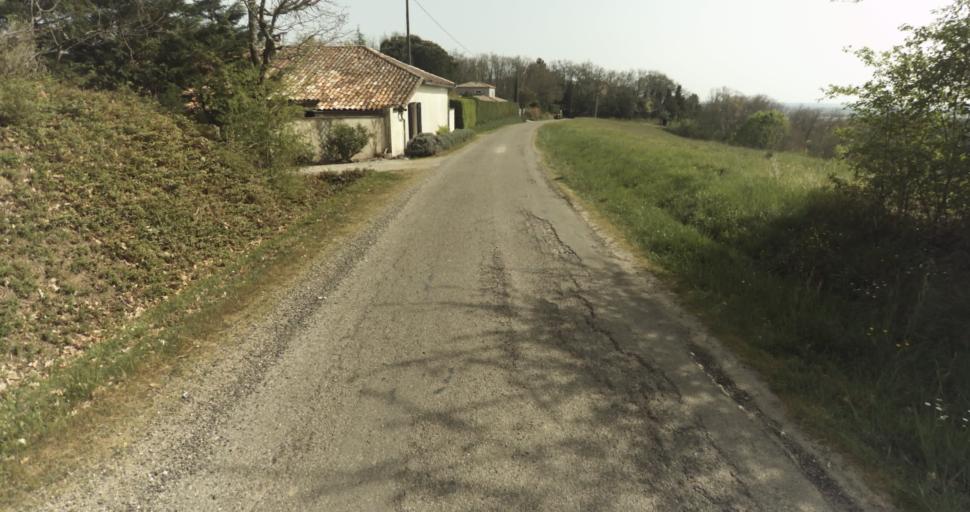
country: FR
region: Midi-Pyrenees
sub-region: Departement du Tarn-et-Garonne
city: Moissac
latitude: 44.1356
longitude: 1.1466
